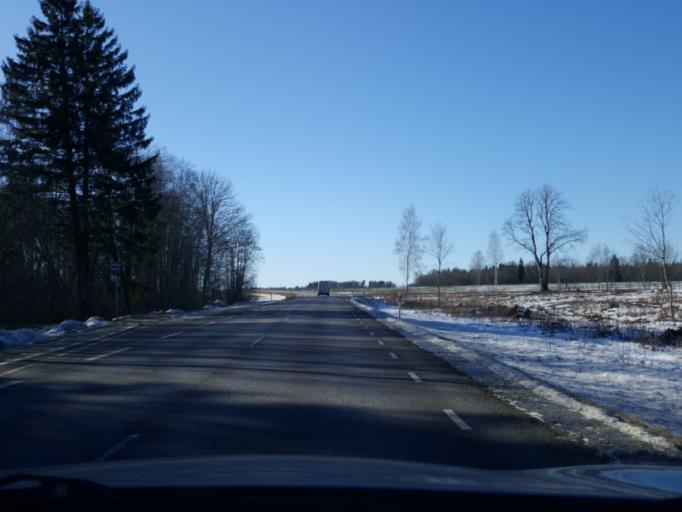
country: EE
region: Viljandimaa
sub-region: Viiratsi vald
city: Viiratsi
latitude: 58.4148
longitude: 25.6711
